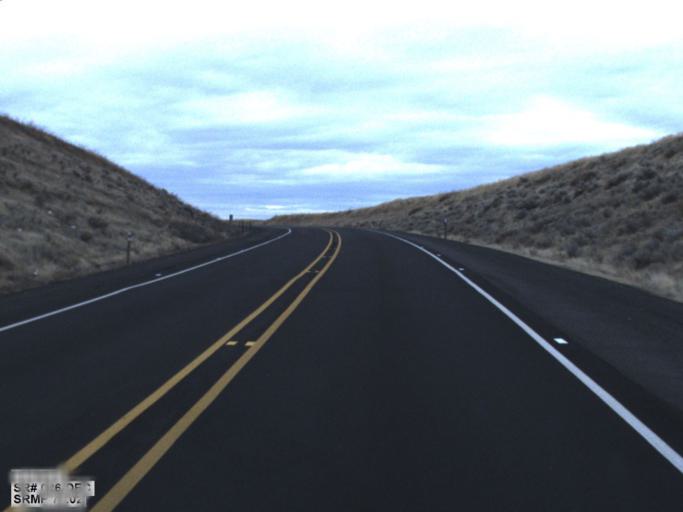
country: US
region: Washington
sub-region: Adams County
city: Ritzville
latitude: 46.7937
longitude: -118.3913
